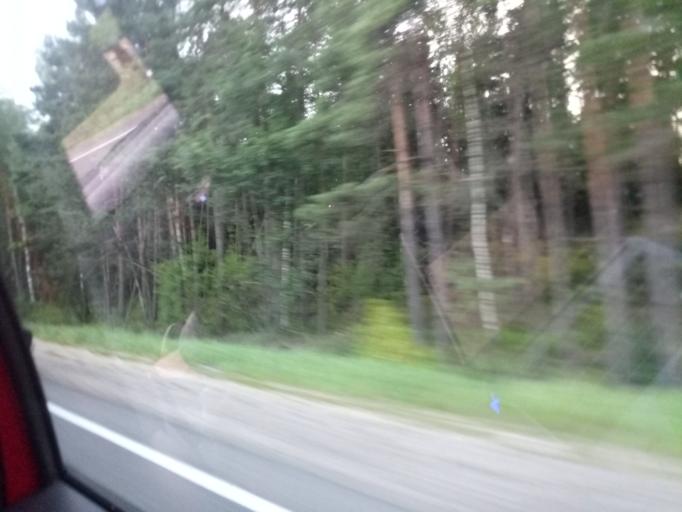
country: RU
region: Moskovskaya
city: Noginsk-9
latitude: 56.0896
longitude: 38.5795
